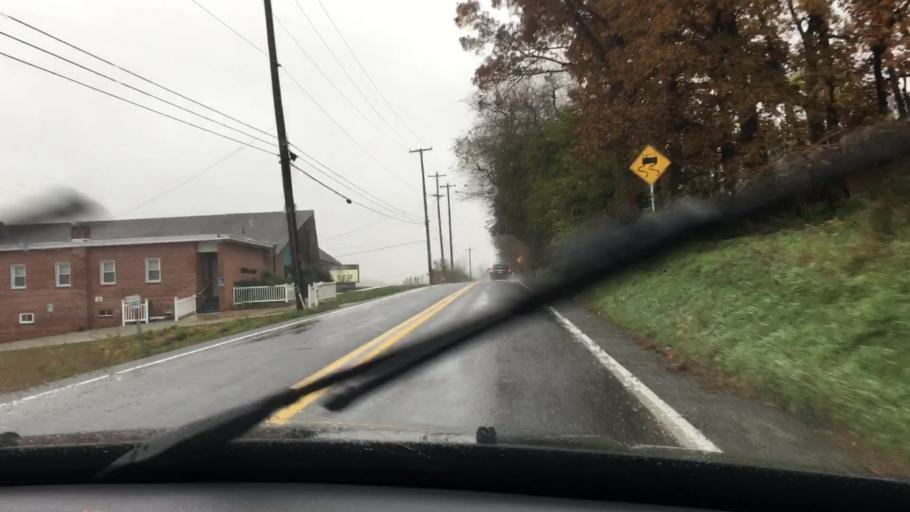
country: US
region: Pennsylvania
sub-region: York County
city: Glen Rock
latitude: 39.7496
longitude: -76.7914
